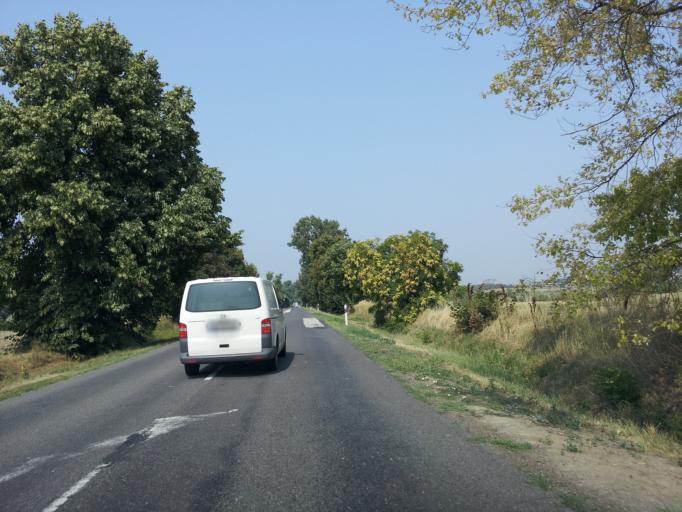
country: HU
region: Gyor-Moson-Sopron
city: Pannonhalma
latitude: 47.4951
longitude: 17.7779
